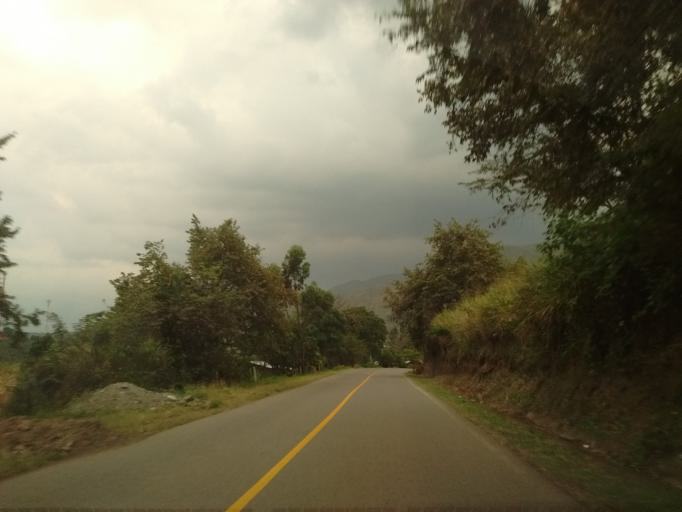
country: CO
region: Cauca
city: Caloto
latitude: 3.0659
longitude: -76.3608
